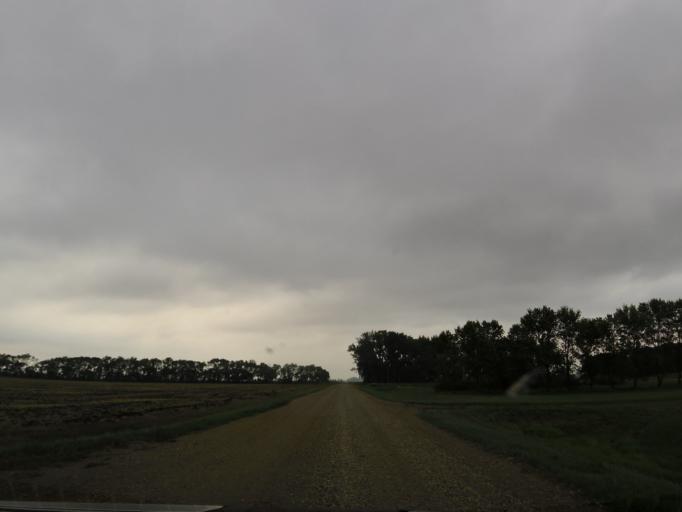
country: US
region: North Dakota
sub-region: Walsh County
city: Grafton
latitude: 48.5033
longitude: -97.1688
